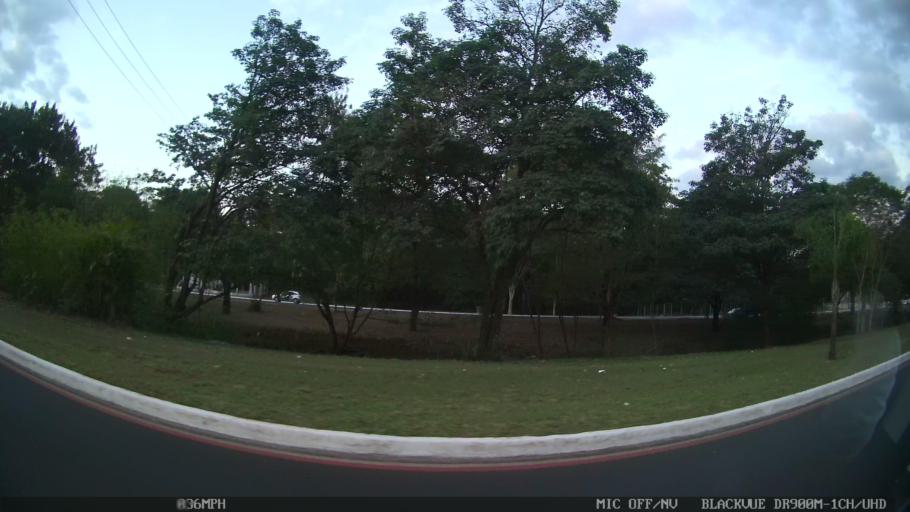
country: BR
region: Sao Paulo
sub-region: Ribeirao Preto
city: Ribeirao Preto
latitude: -21.2008
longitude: -47.7958
